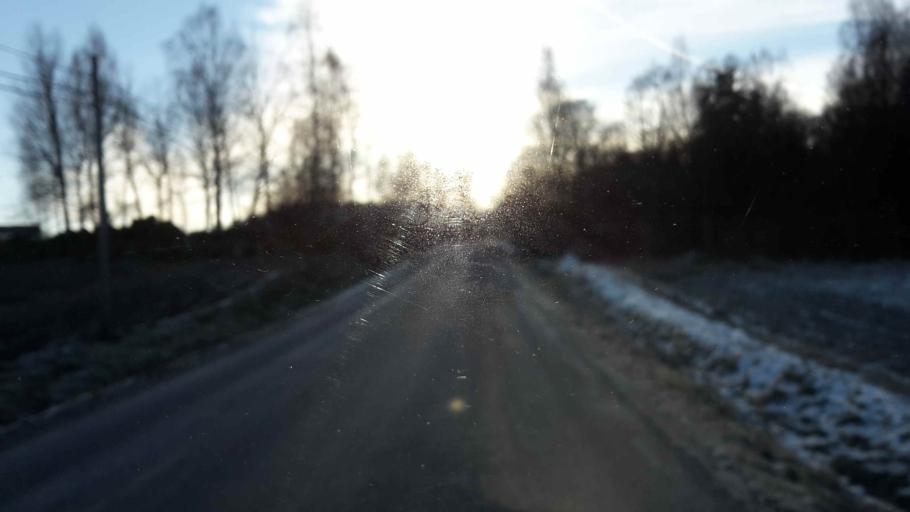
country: SE
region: OEstergoetland
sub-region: Atvidabergs Kommun
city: Atvidaberg
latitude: 58.2382
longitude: 16.0826
